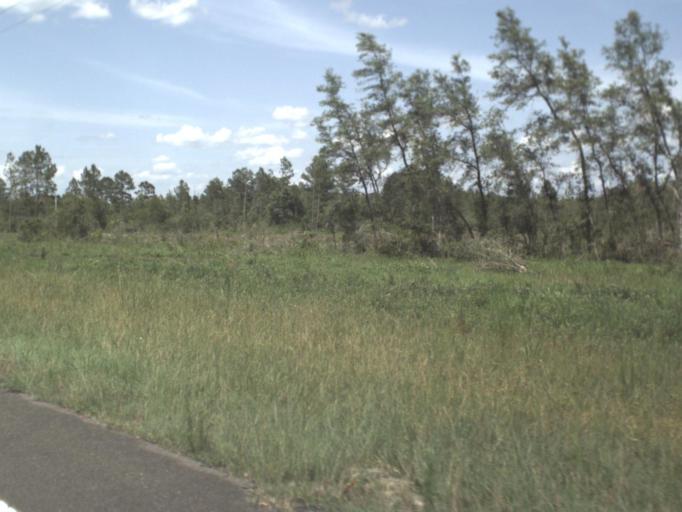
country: US
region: Florida
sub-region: Gilchrist County
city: Trenton
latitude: 29.6928
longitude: -82.7625
